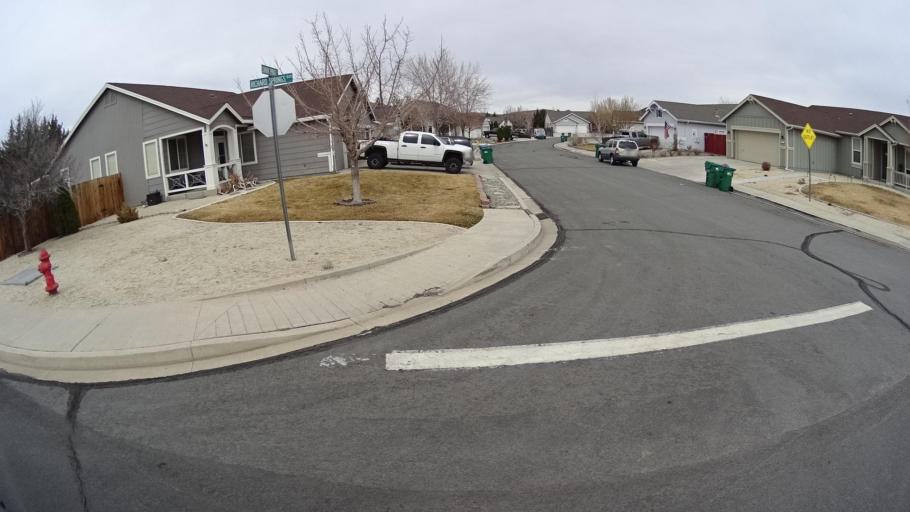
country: US
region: Nevada
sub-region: Washoe County
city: Spanish Springs
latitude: 39.6349
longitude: -119.7279
